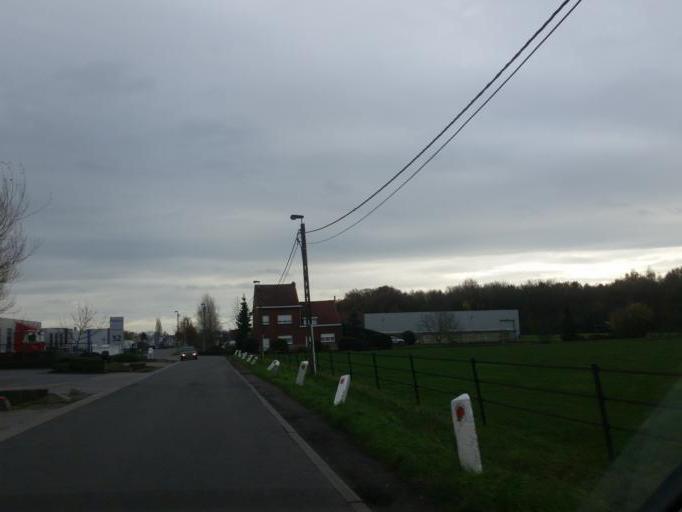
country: BE
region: Flanders
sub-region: Provincie Antwerpen
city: Sint-Katelijne-Waver
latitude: 51.0694
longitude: 4.5096
